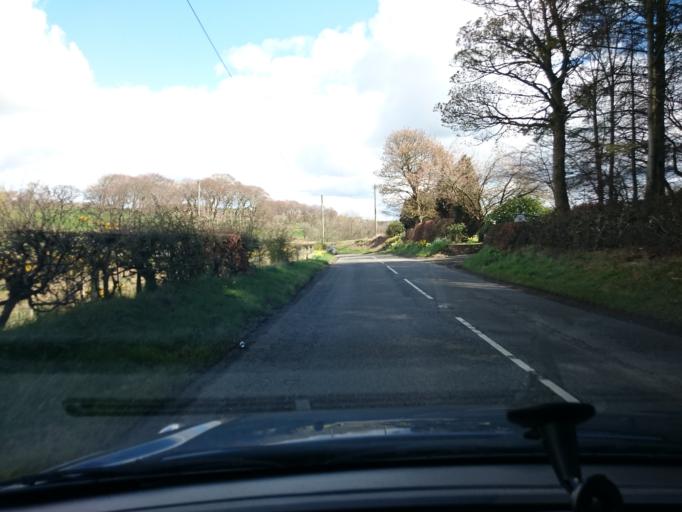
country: GB
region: Scotland
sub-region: Falkirk
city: Falkirk
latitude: 55.9815
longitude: -3.8156
